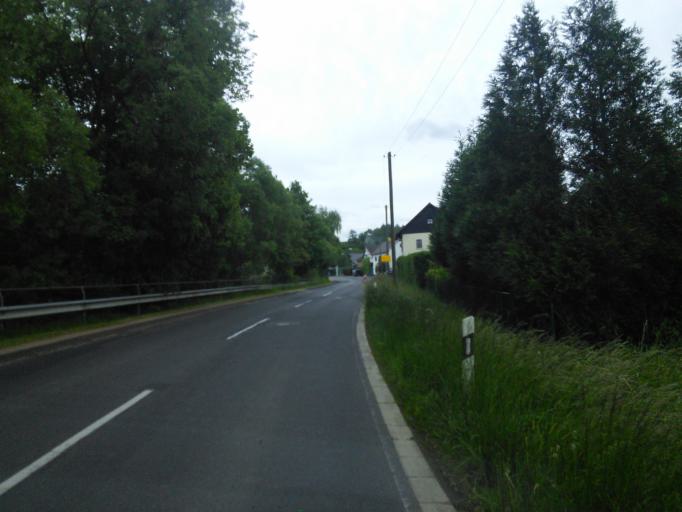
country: DE
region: North Rhine-Westphalia
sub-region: Regierungsbezirk Koln
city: Rheinbach
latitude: 50.5899
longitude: 6.8993
